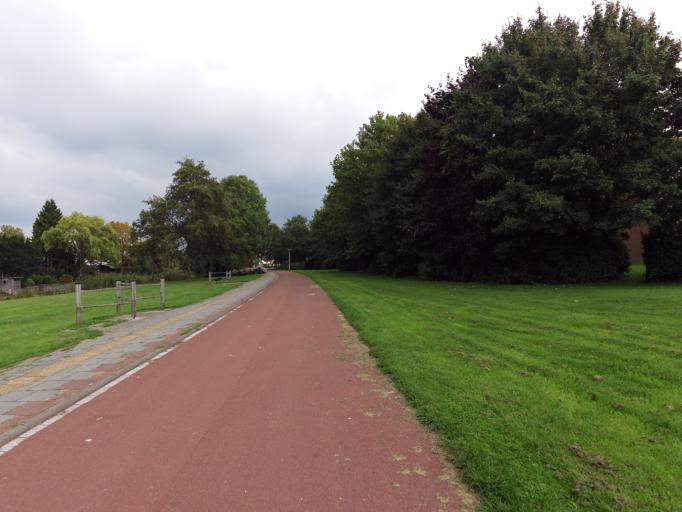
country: NL
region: Gelderland
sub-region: Gemeente Westervoort
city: Westervoort
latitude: 51.9455
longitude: 5.9731
